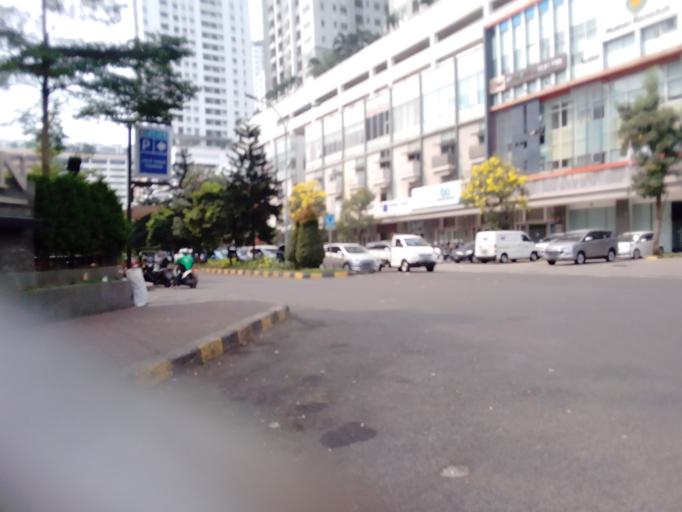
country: ID
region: Jakarta Raya
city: Jakarta
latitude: -6.1978
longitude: 106.8159
